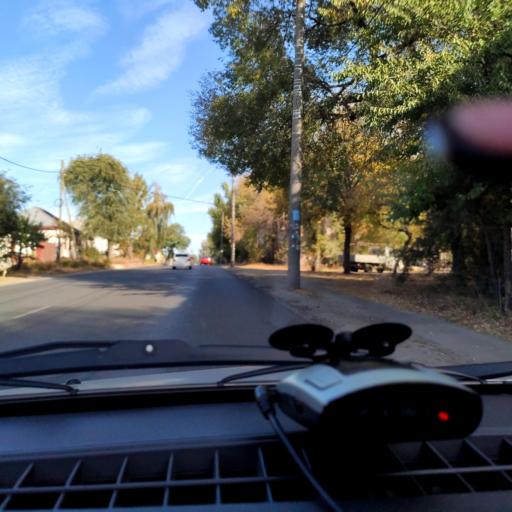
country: RU
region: Voronezj
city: Voronezh
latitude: 51.6955
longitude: 39.1644
